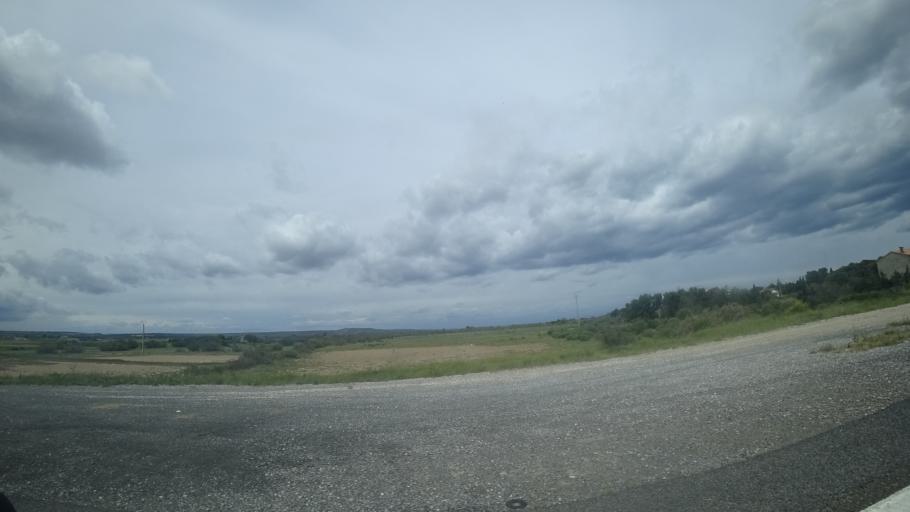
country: FR
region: Languedoc-Roussillon
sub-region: Departement de l'Aude
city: Leucate
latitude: 42.9319
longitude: 3.0099
